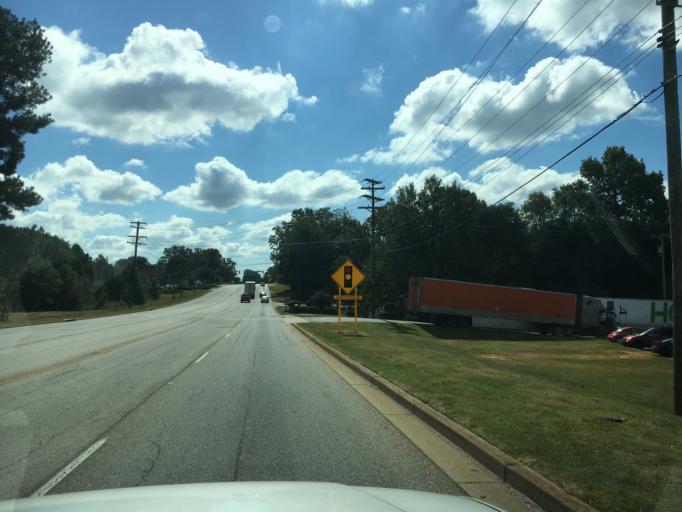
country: US
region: South Carolina
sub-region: Greenville County
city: Greer
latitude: 34.9167
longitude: -82.2407
